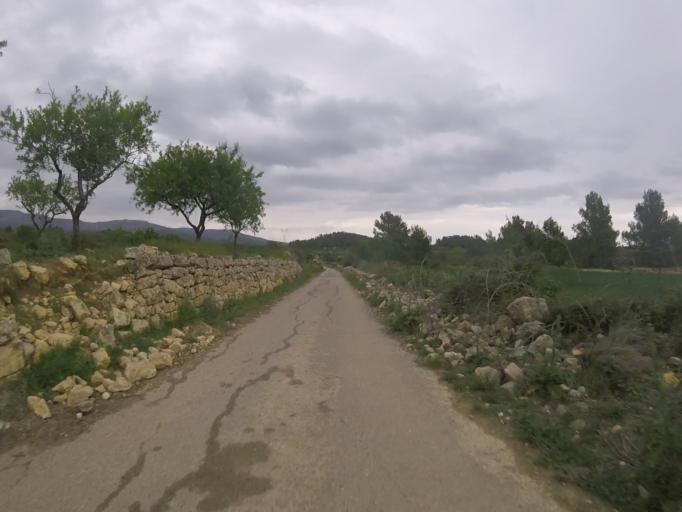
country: ES
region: Valencia
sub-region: Provincia de Castello
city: Sarratella
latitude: 40.2706
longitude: 0.0707
